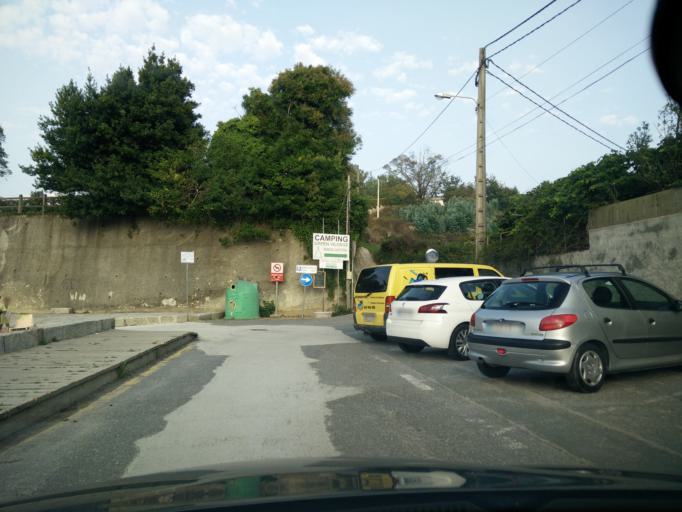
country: ES
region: Galicia
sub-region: Provincia da Coruna
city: Bergondo
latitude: 43.3418
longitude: -8.2338
